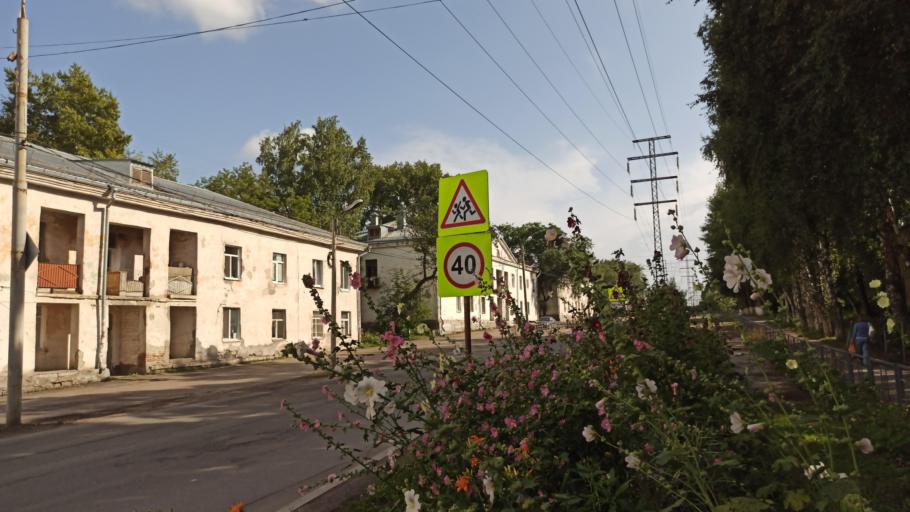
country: RU
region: Tomsk
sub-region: Tomskiy Rayon
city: Tomsk
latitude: 56.4806
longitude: 84.9998
